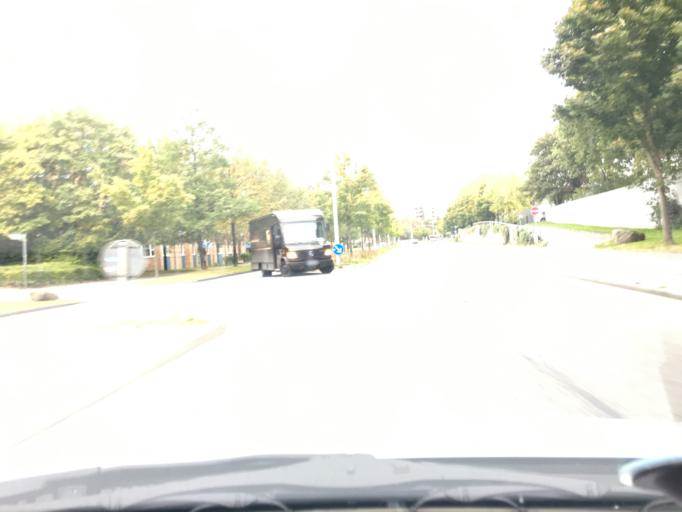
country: DE
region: Schleswig-Holstein
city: Melsdorf
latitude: 54.3223
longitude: 10.0521
